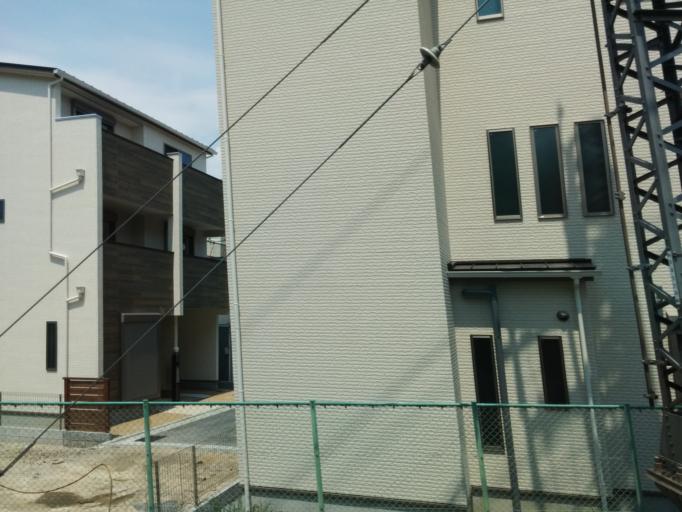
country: JP
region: Osaka
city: Suita
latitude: 34.7423
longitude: 135.5205
